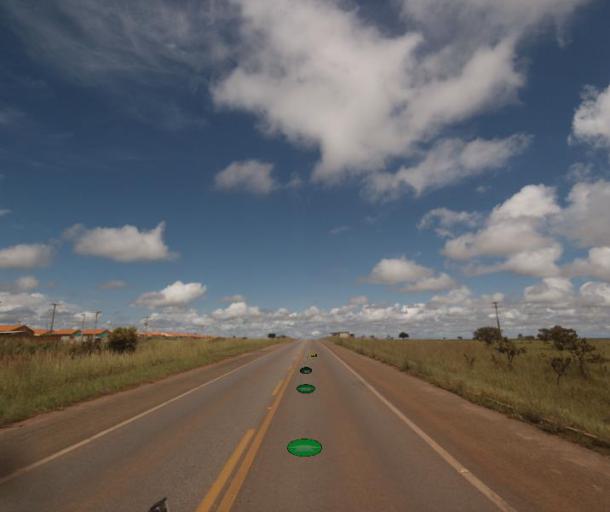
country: BR
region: Federal District
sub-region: Brasilia
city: Brasilia
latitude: -15.7455
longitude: -48.4109
